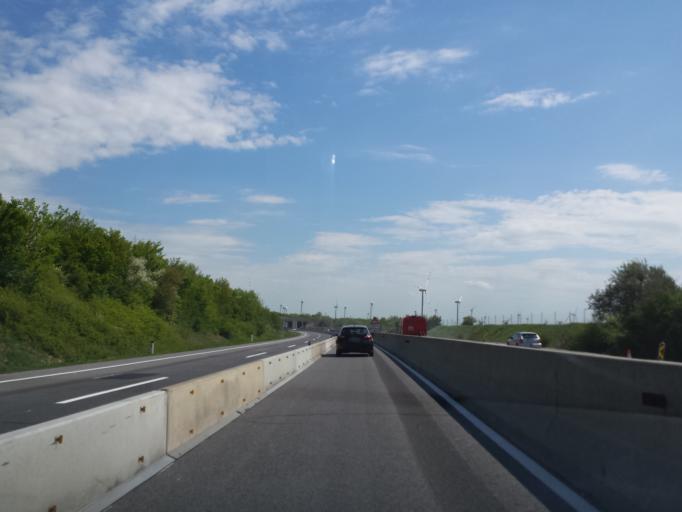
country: AT
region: Burgenland
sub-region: Politischer Bezirk Neusiedl am See
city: Gols
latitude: 47.9458
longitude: 16.9380
